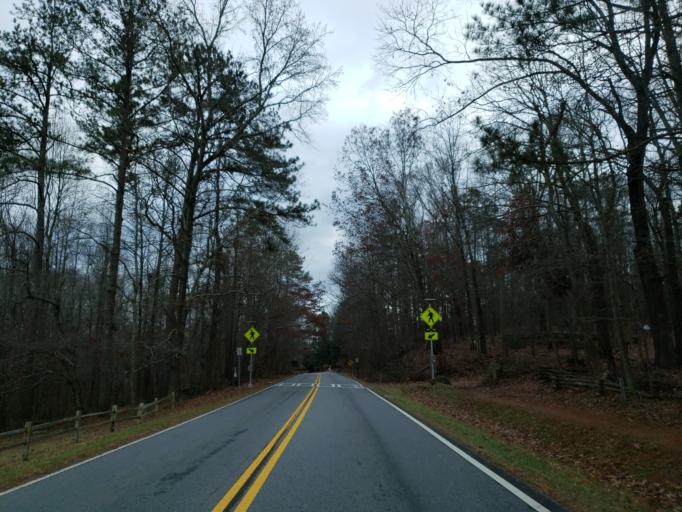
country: US
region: Georgia
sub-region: Cobb County
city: Marietta
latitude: 33.9324
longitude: -84.6043
